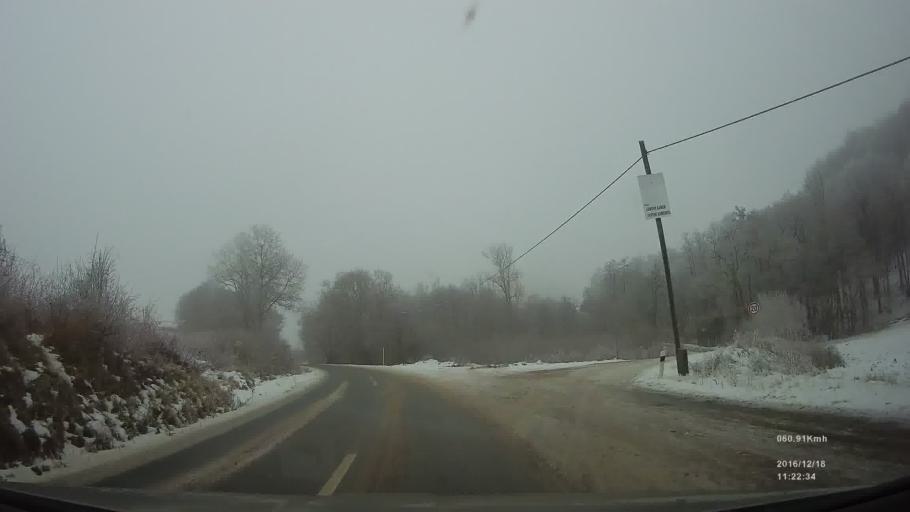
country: SK
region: Presovsky
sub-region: Okres Presov
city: Presov
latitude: 48.9009
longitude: 21.3801
